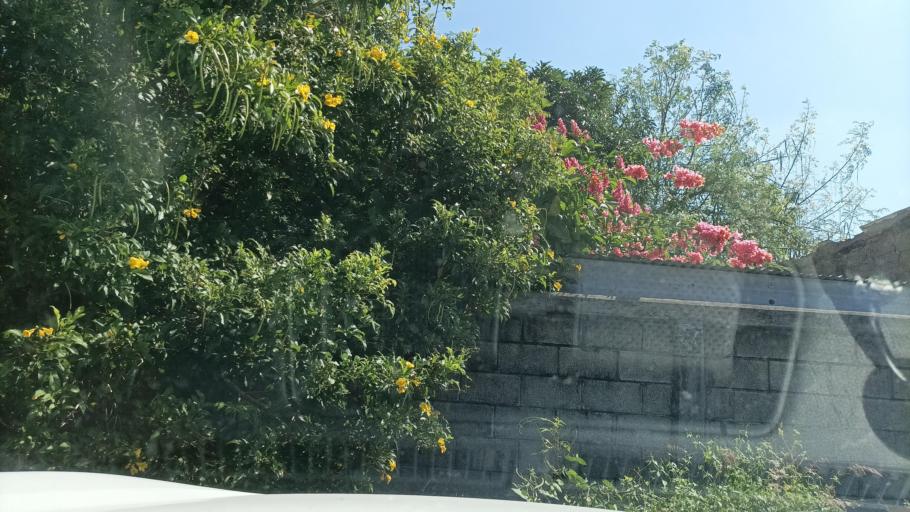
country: MX
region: Veracruz
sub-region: Veracruz
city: Rio Medio [Granja]
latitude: 19.1997
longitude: -96.1790
